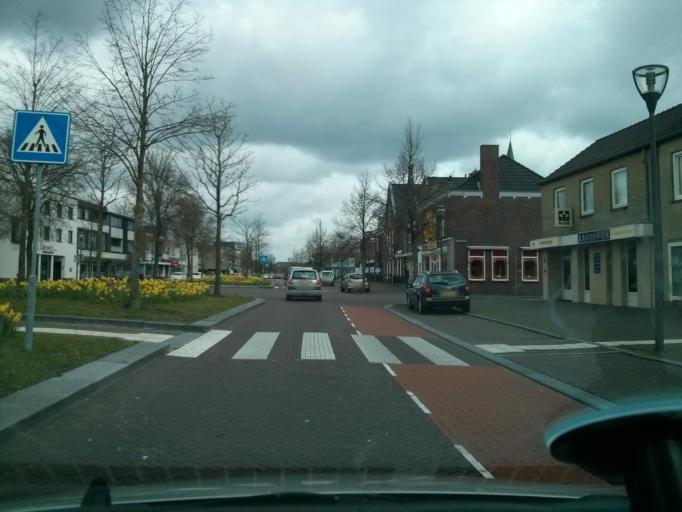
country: NL
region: North Brabant
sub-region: Gemeente Son en Breugel
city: Son
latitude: 51.5087
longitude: 5.4922
